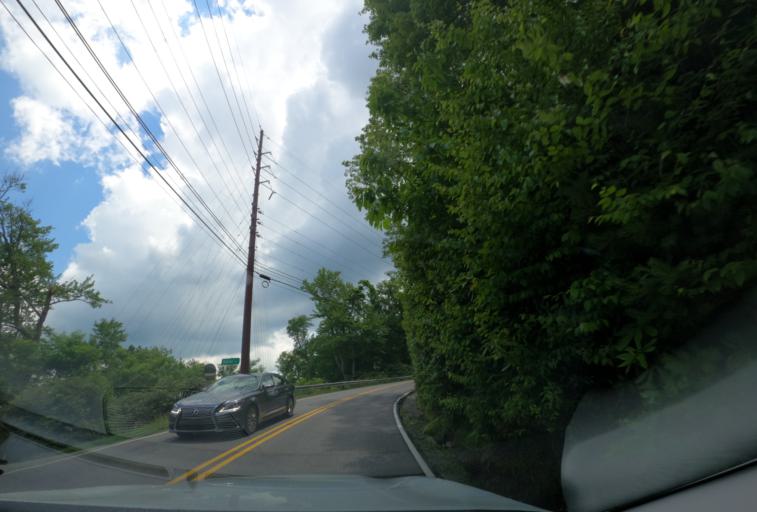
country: US
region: North Carolina
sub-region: Jackson County
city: Cullowhee
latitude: 35.0885
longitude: -83.1695
